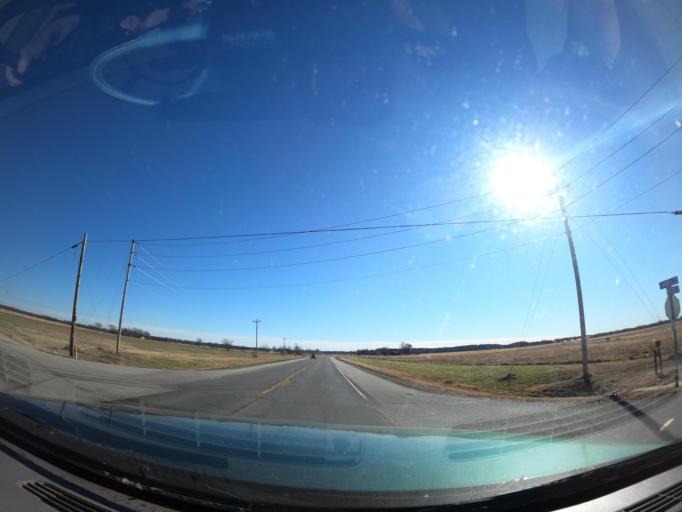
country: US
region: Oklahoma
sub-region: Muskogee County
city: Haskell
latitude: 35.7985
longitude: -95.6700
